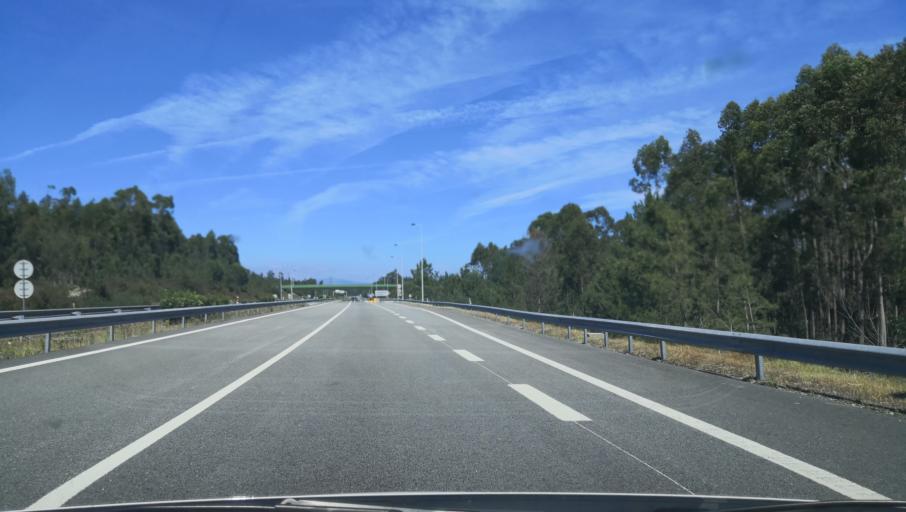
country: PT
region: Coimbra
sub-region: Montemor-O-Velho
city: Arazede
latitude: 40.2579
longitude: -8.6330
